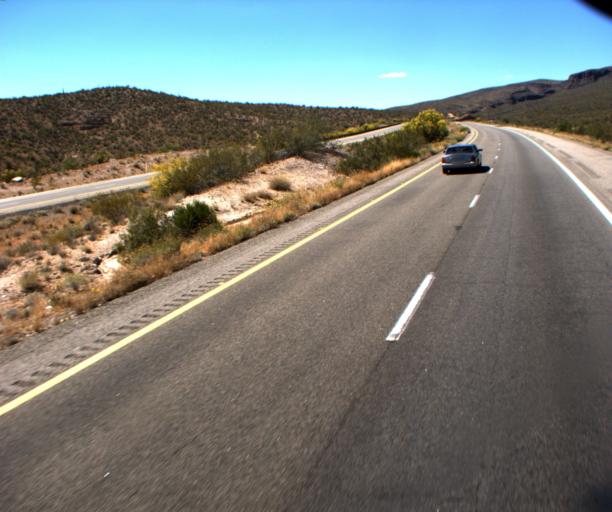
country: US
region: Arizona
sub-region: Yavapai County
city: Bagdad
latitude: 34.5546
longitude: -113.4532
